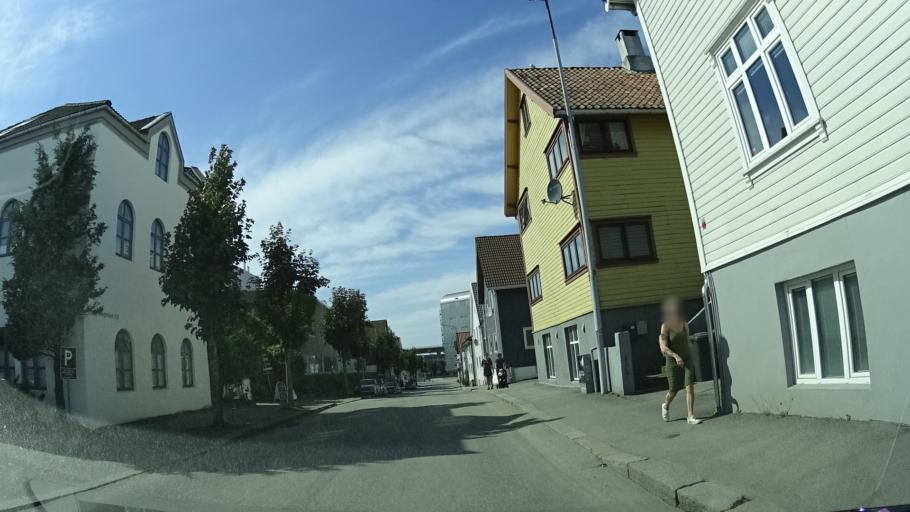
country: NO
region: Rogaland
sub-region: Stavanger
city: Stavanger
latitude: 58.9691
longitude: 5.7537
